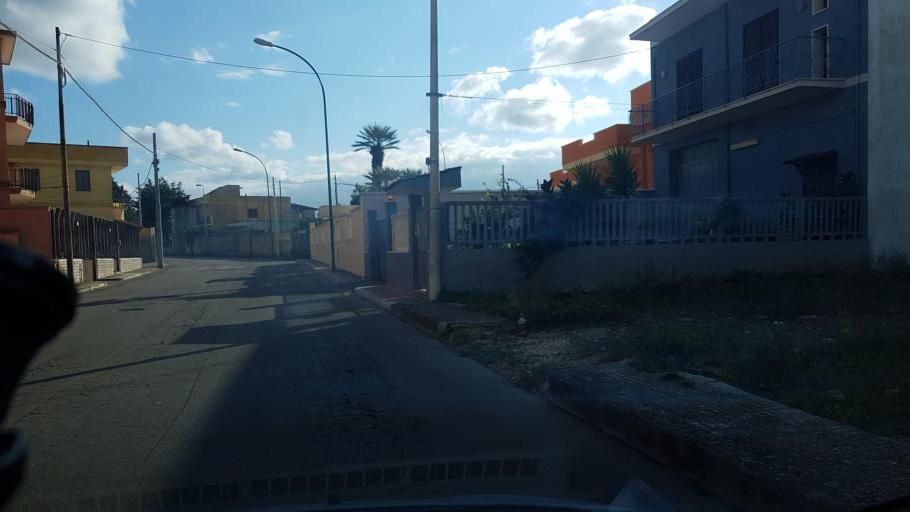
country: IT
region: Apulia
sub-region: Provincia di Lecce
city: Squinzano
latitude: 40.4329
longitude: 18.0315
